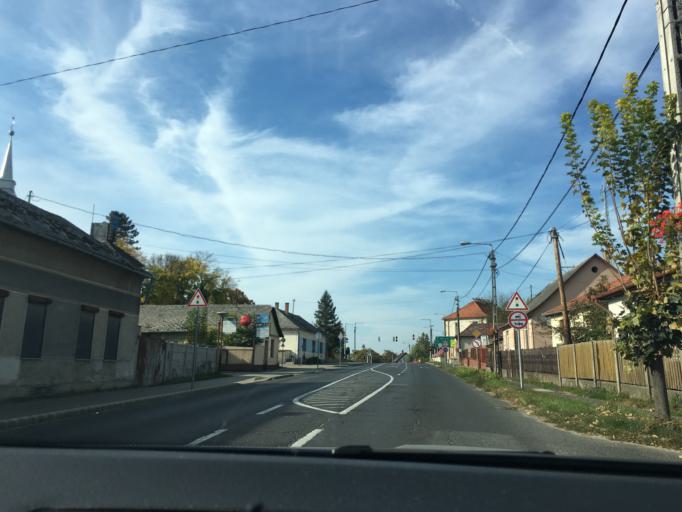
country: HU
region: Hajdu-Bihar
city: Vamospercs
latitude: 47.5260
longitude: 21.8998
